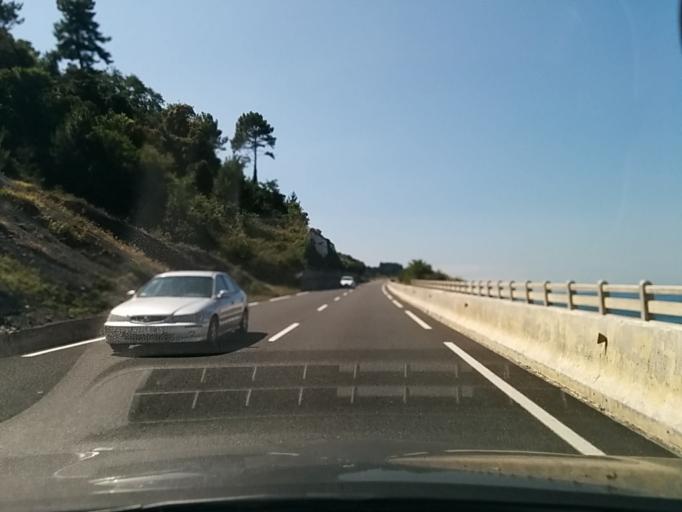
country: ES
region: Basque Country
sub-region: Provincia de Guipuzcoa
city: Deba
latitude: 43.3041
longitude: -2.3601
